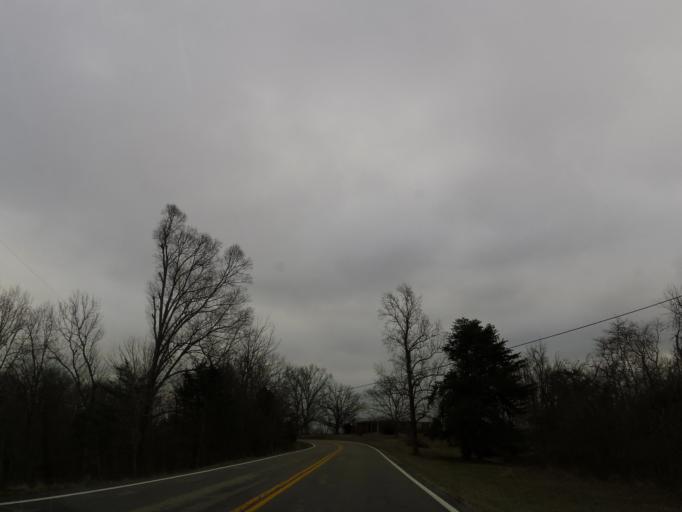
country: US
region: Kentucky
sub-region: Franklin County
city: Frankfort
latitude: 38.3338
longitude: -84.9555
